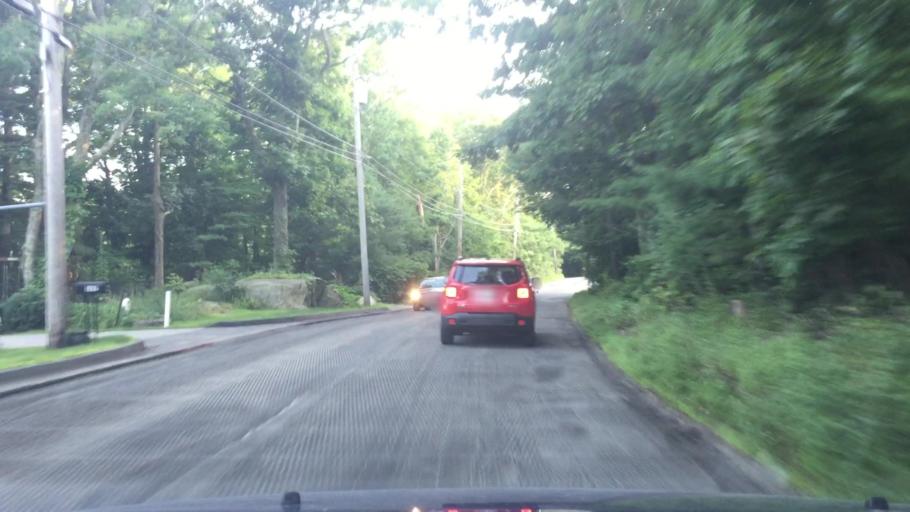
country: US
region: Massachusetts
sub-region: Middlesex County
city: Hopkinton
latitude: 42.1920
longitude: -71.5043
